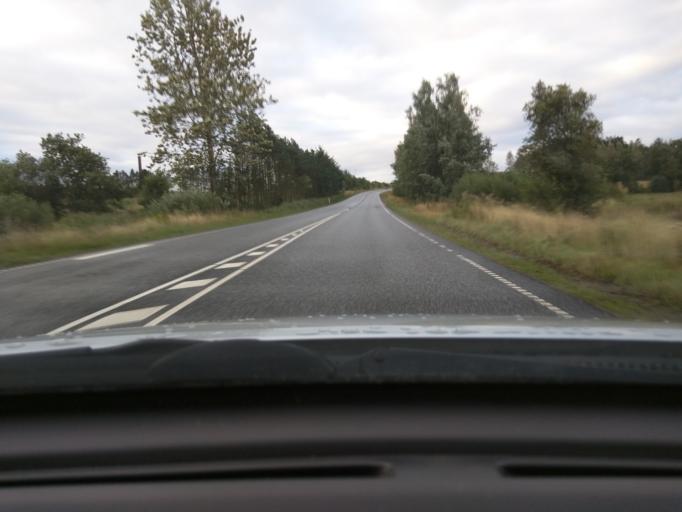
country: DK
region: Central Jutland
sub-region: Silkeborg Kommune
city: Kjellerup
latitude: 56.3253
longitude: 9.3331
